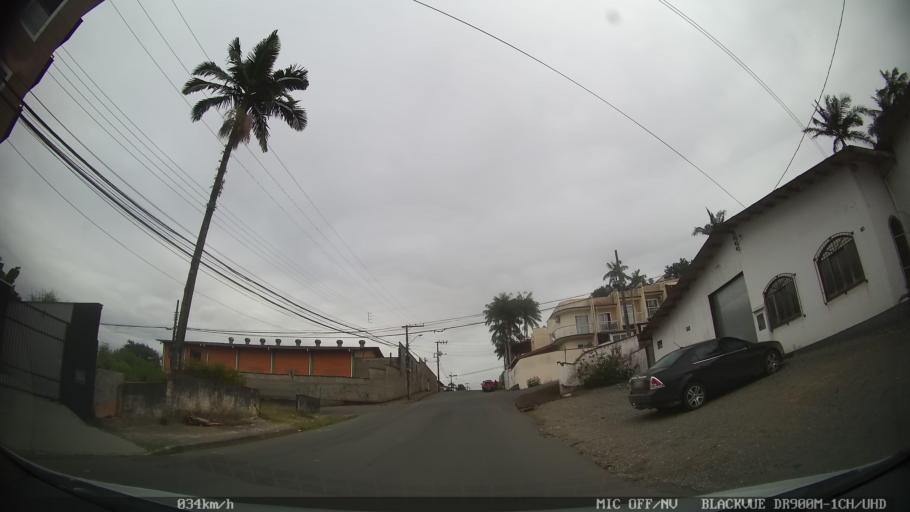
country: BR
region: Santa Catarina
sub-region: Joinville
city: Joinville
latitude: -26.2683
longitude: -48.8848
